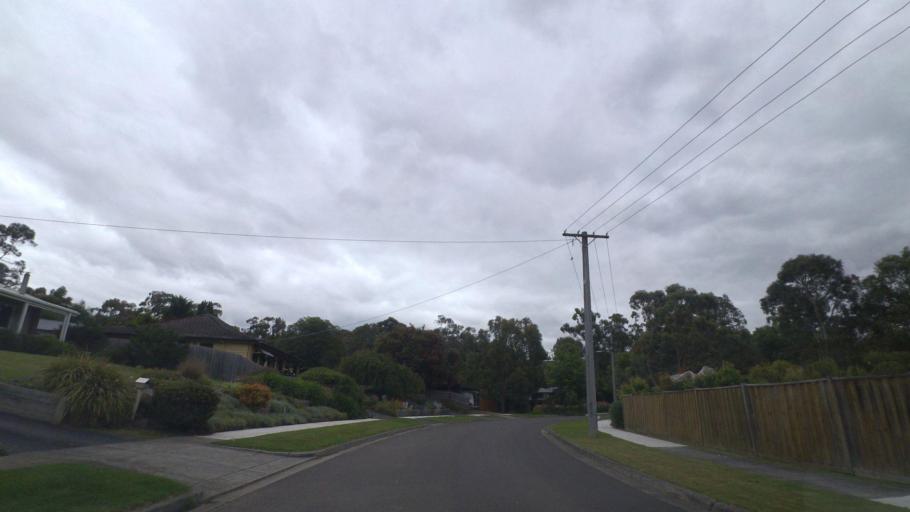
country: AU
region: Victoria
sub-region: Yarra Ranges
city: Mount Evelyn
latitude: -37.7745
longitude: 145.4300
